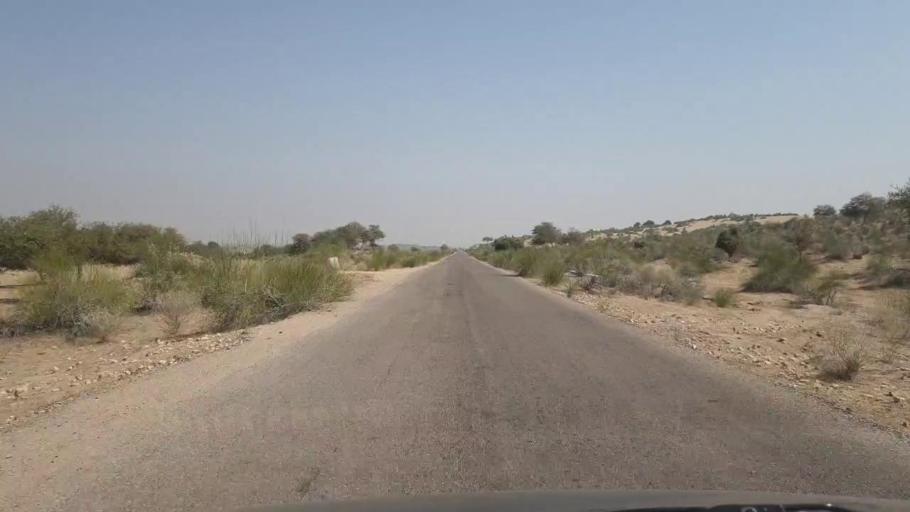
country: PK
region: Sindh
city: Chor
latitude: 25.6649
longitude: 70.1341
